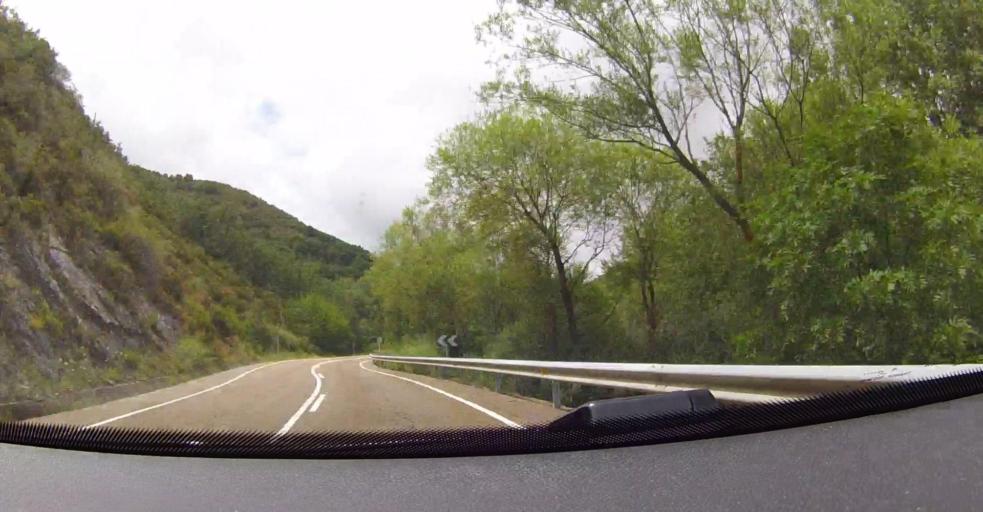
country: ES
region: Castille and Leon
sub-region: Provincia de Leon
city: Bonar
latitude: 42.8969
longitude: -5.3104
